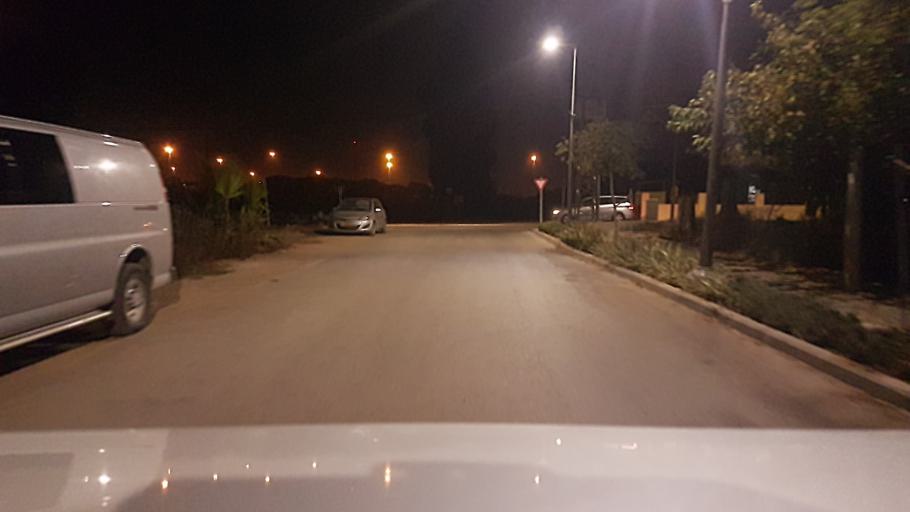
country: IL
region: Central District
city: Nehalim
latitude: 32.0741
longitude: 34.9304
